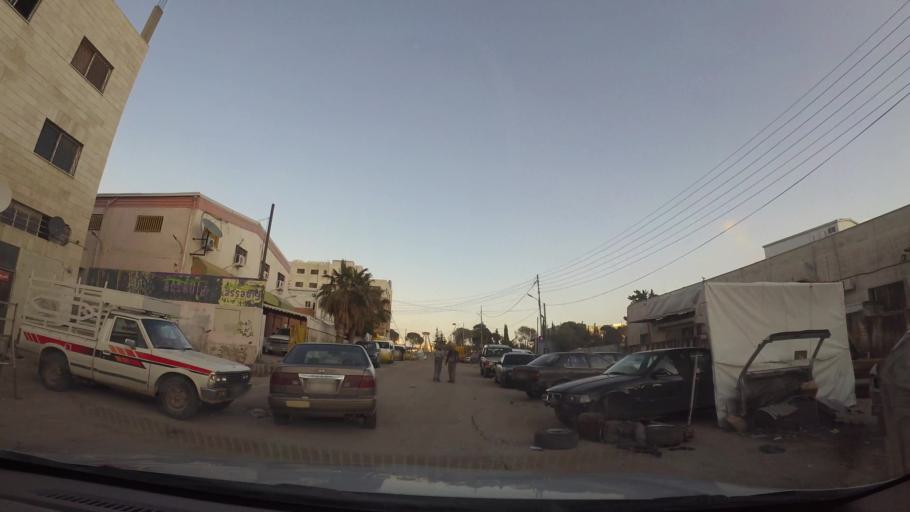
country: JO
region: Amman
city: Al Bunayyat ash Shamaliyah
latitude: 31.9129
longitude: 35.9156
